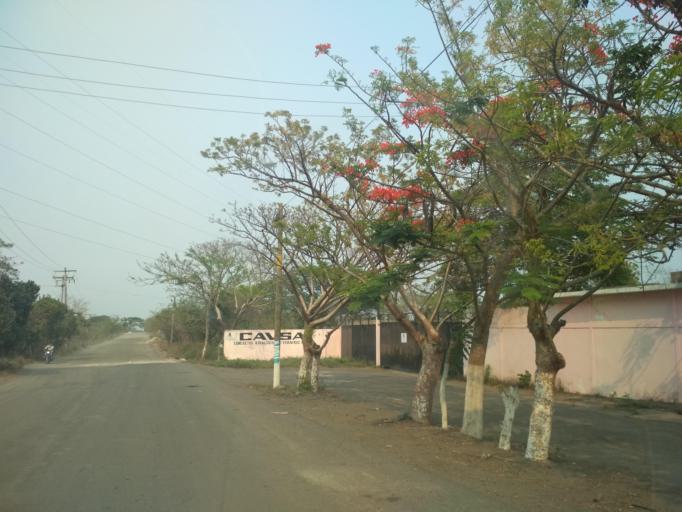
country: MX
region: Veracruz
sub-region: Veracruz
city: Las Amapolas
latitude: 19.1460
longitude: -96.2410
